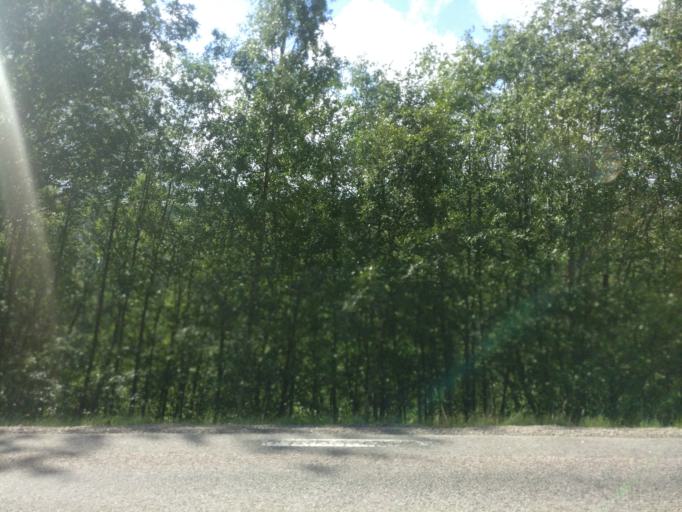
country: SE
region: Vaermland
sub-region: Hagfors Kommun
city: Ekshaerad
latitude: 60.3694
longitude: 13.3052
